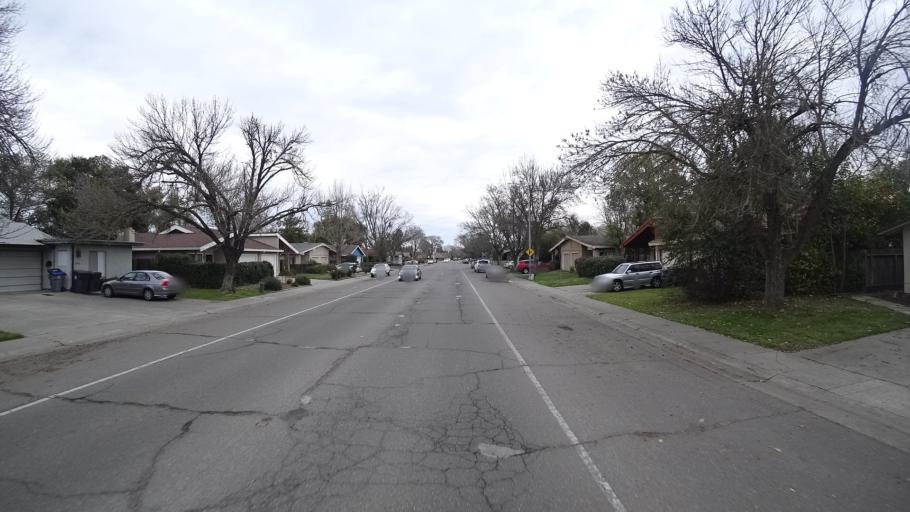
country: US
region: California
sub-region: Yolo County
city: Davis
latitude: 38.5540
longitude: -121.7242
